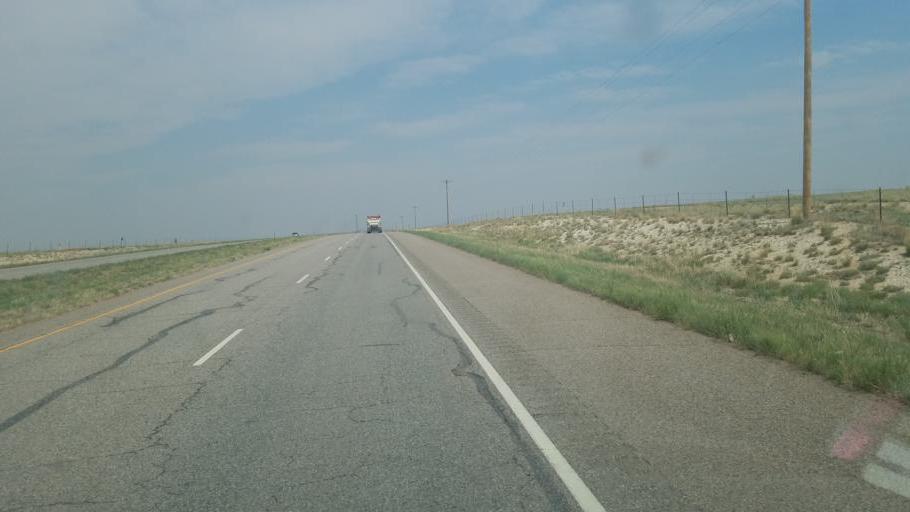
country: US
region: Colorado
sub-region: Fremont County
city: Penrose
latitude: 38.3648
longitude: -104.8986
